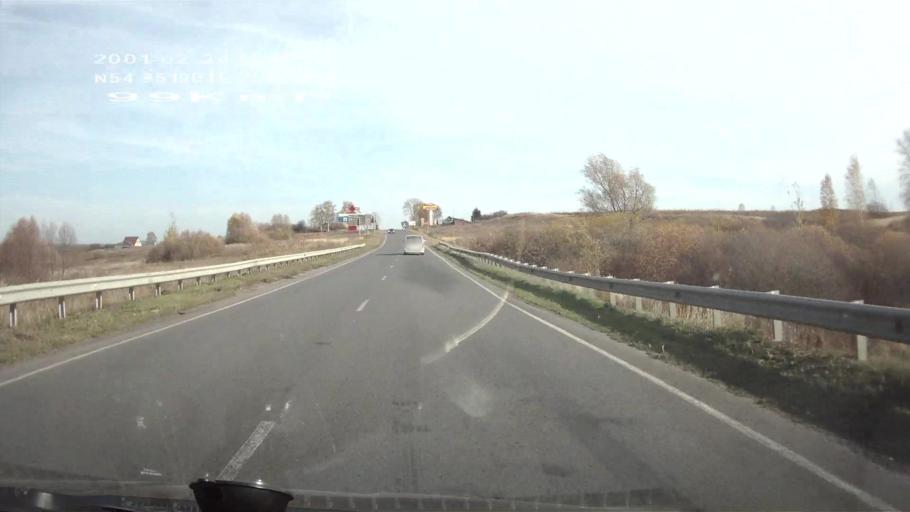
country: RU
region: Mordoviya
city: Turgenevo
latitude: 54.8519
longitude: 46.3911
